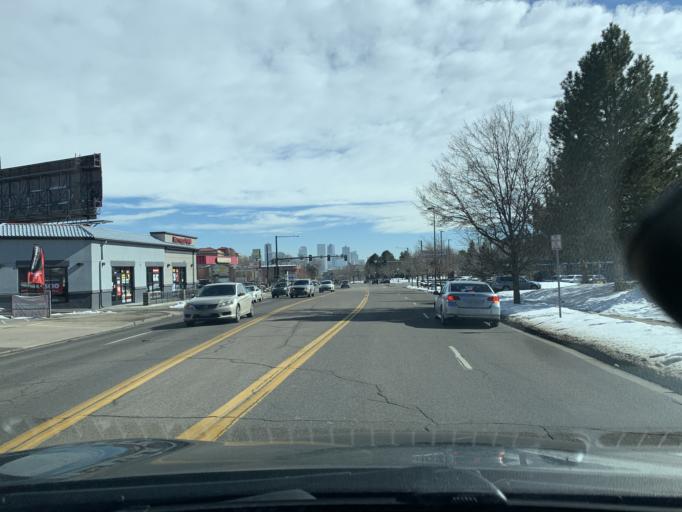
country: US
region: Colorado
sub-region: Jefferson County
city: Edgewater
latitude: 39.7609
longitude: -105.0265
